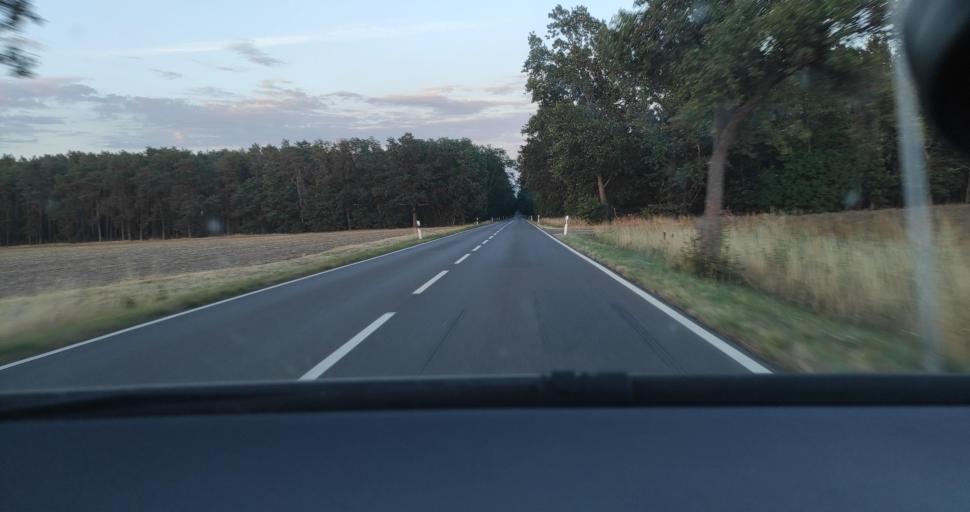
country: DE
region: Brandenburg
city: Forst
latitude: 51.7244
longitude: 14.5478
